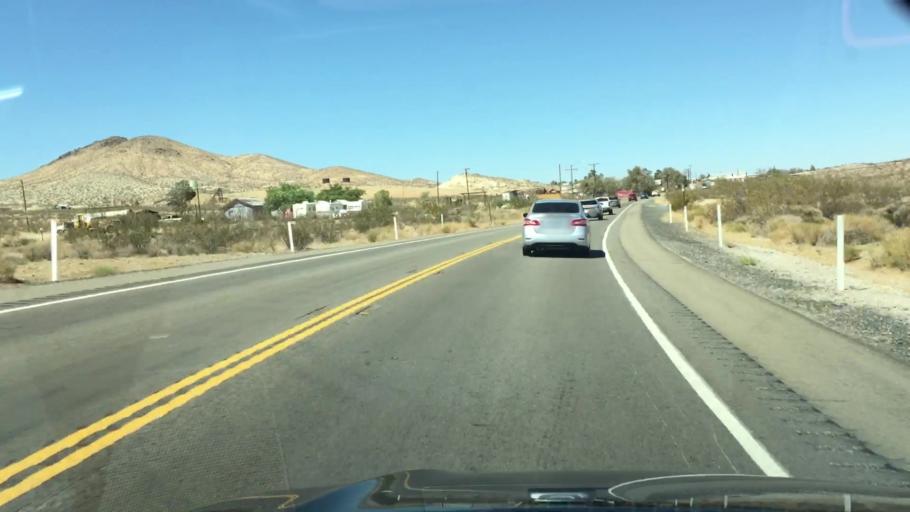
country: US
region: California
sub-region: Kern County
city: Ridgecrest
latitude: 35.3490
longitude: -117.6178
